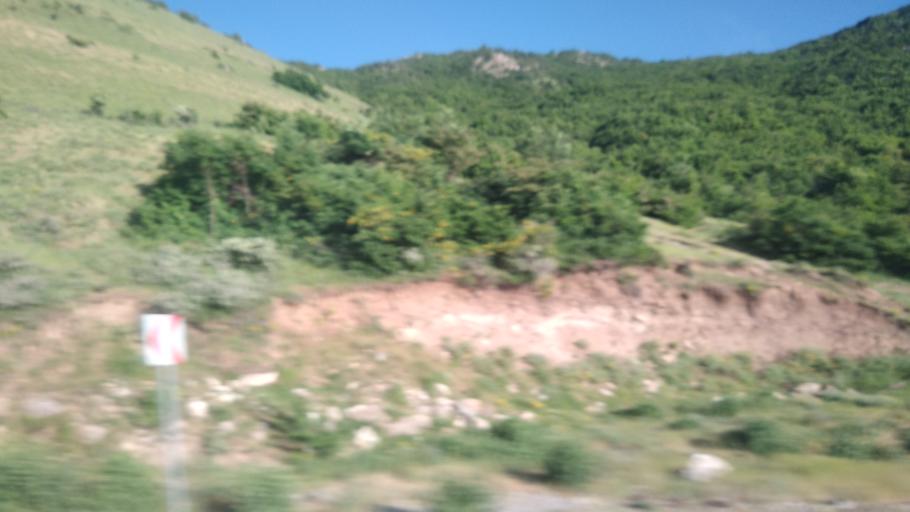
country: TR
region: Bitlis
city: Resadiye
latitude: 38.4771
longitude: 42.5348
